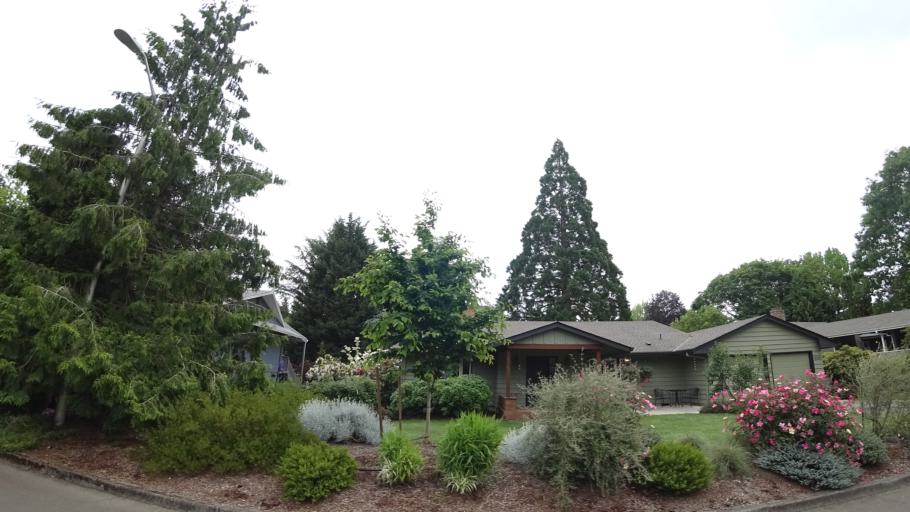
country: US
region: Oregon
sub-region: Washington County
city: Garden Home-Whitford
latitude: 45.4654
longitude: -122.7736
